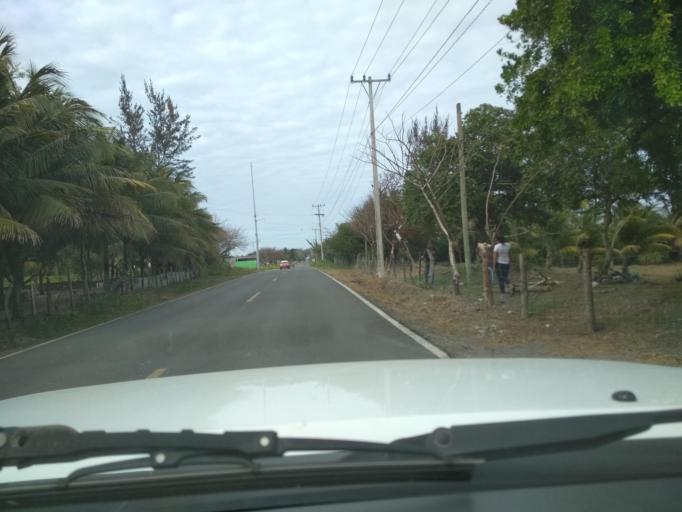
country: MX
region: Veracruz
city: Anton Lizardo
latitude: 19.0475
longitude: -95.9865
